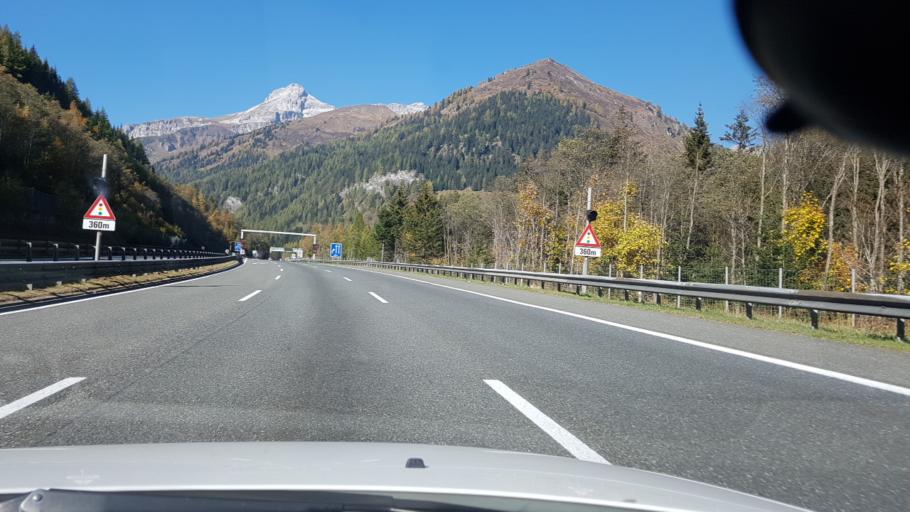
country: AT
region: Salzburg
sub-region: Politischer Bezirk Tamsweg
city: Zederhaus
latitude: 47.1774
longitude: 13.4450
